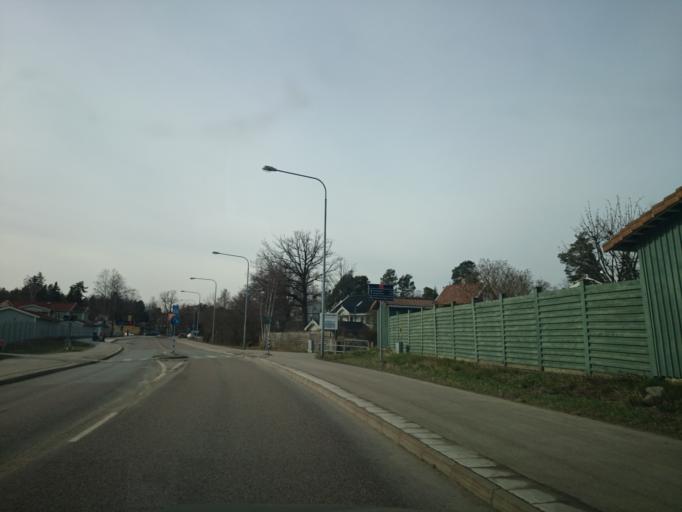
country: SE
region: Stockholm
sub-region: Huddinge Kommun
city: Huddinge
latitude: 59.2589
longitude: 17.9778
